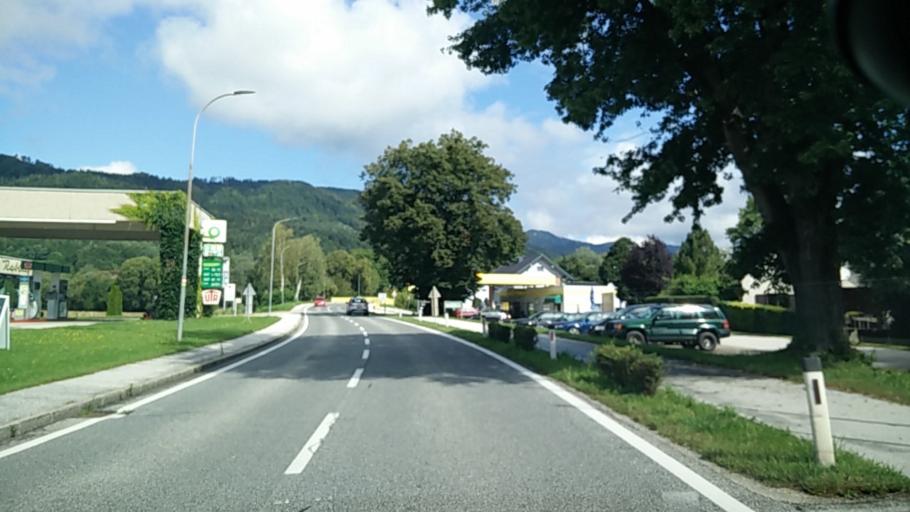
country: AT
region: Carinthia
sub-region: Politischer Bezirk Sankt Veit an der Glan
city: Bruckl
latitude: 46.7459
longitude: 14.5315
